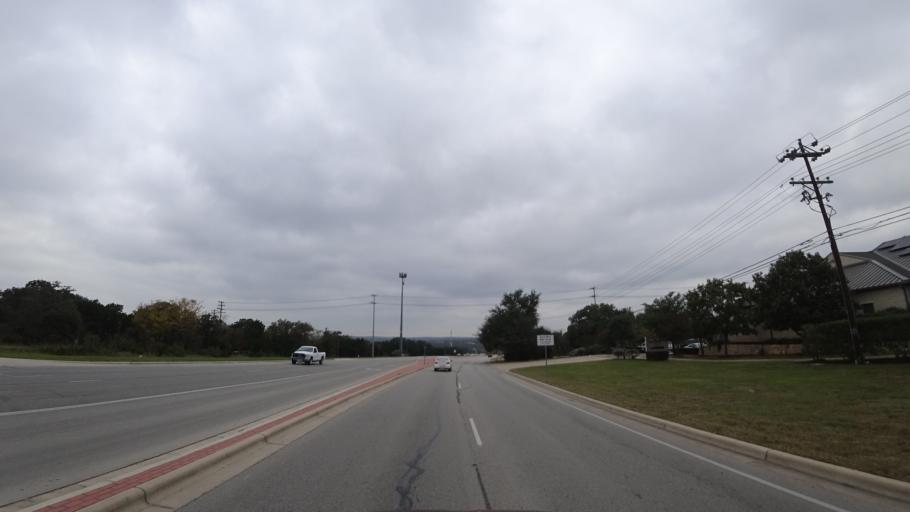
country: US
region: Texas
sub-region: Williamson County
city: Anderson Mill
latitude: 30.4560
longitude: -97.8283
